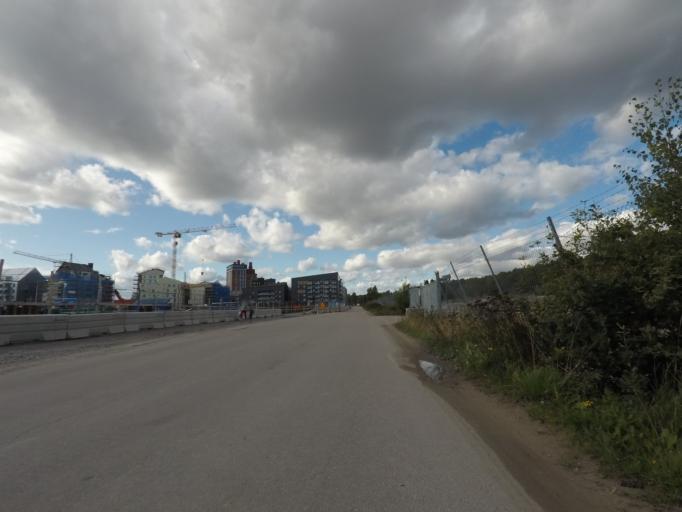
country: SE
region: Vaestmanland
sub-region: Vasteras
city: Vasteras
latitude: 59.6050
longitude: 16.5753
